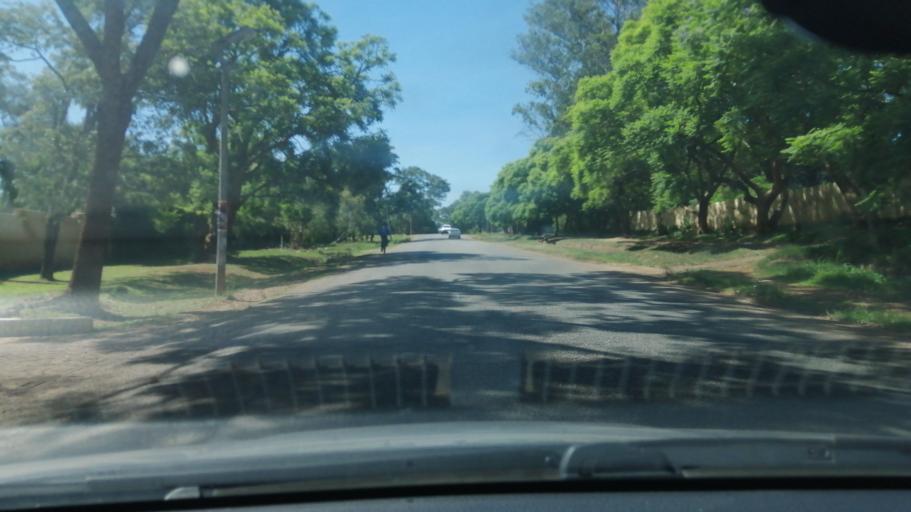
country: ZW
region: Harare
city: Harare
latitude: -17.7991
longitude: 31.1287
